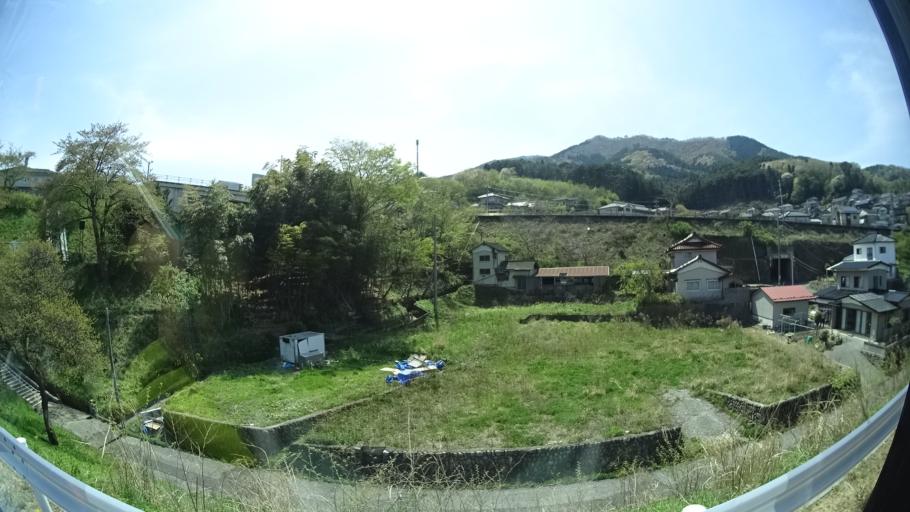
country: JP
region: Iwate
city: Ofunato
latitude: 39.0492
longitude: 141.7216
